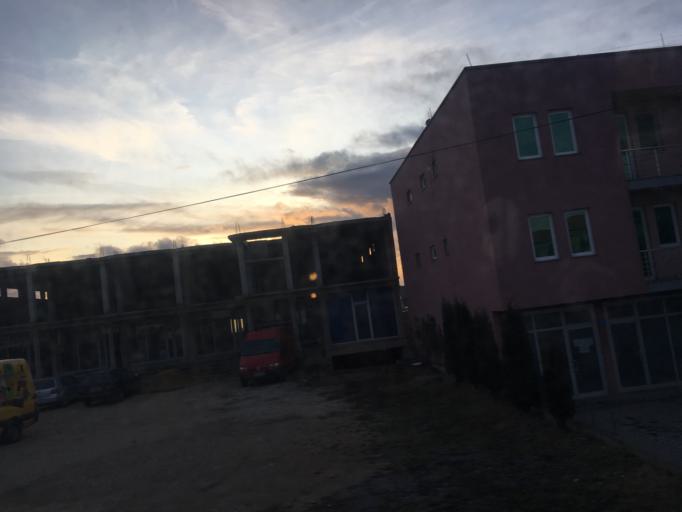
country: XK
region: Pristina
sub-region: Komuna e Drenasit
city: Glogovac
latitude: 42.5819
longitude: 20.8998
